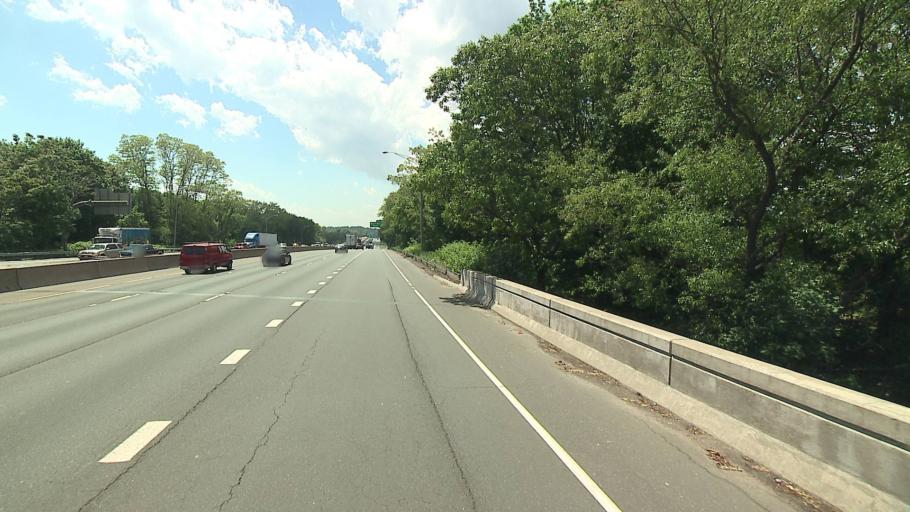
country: US
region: Connecticut
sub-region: Fairfield County
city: Fairfield
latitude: 41.1462
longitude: -73.2596
